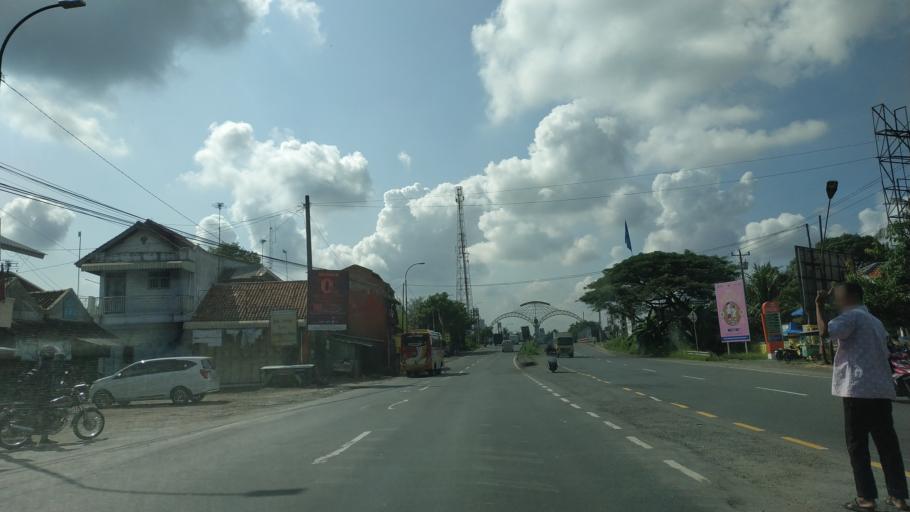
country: ID
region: Central Java
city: Comal
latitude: -6.8839
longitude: 109.5651
